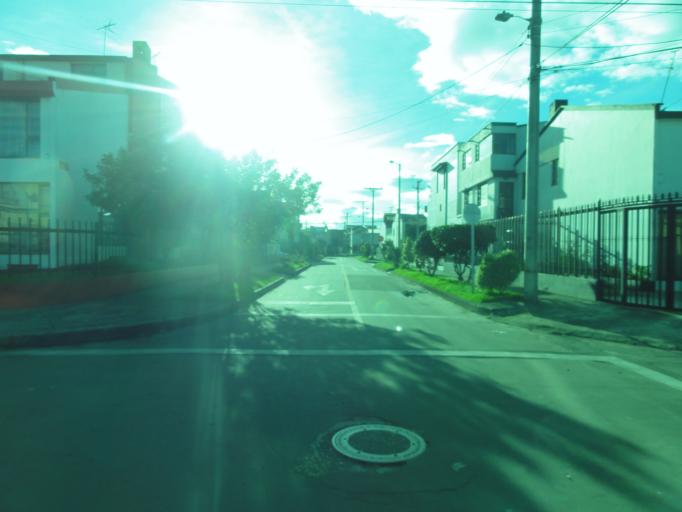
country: CO
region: Bogota D.C.
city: Bogota
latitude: 4.6531
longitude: -74.0852
